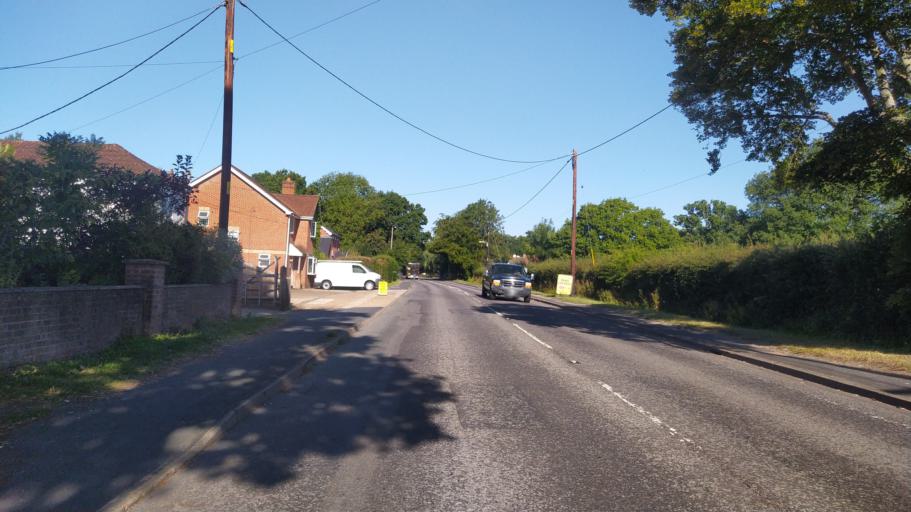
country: GB
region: England
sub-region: Hampshire
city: Totton
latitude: 50.9161
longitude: -1.5334
